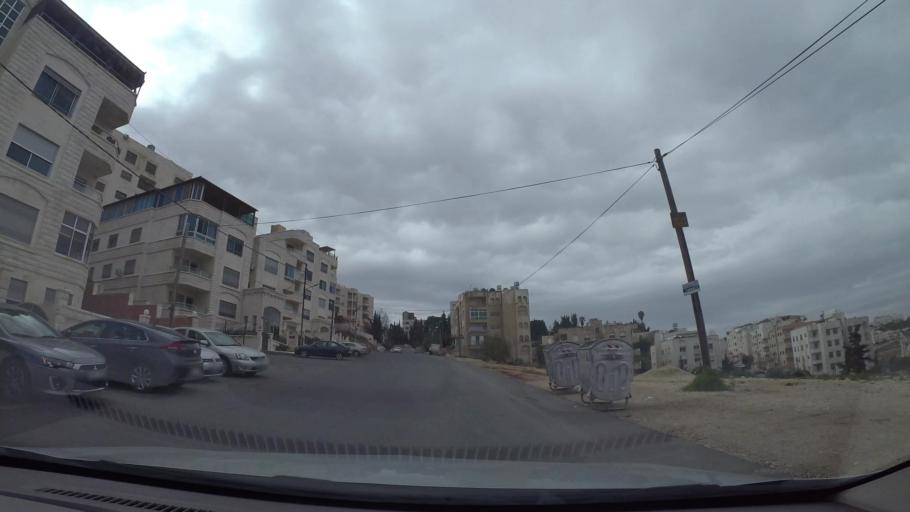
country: JO
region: Amman
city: Al Jubayhah
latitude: 32.0062
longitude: 35.8369
